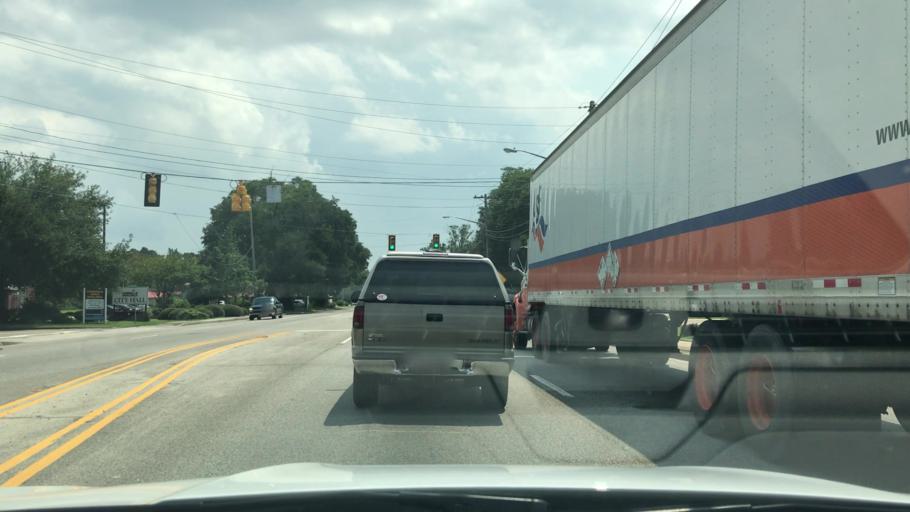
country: US
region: South Carolina
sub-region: Georgetown County
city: Georgetown
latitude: 33.3900
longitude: -79.2891
